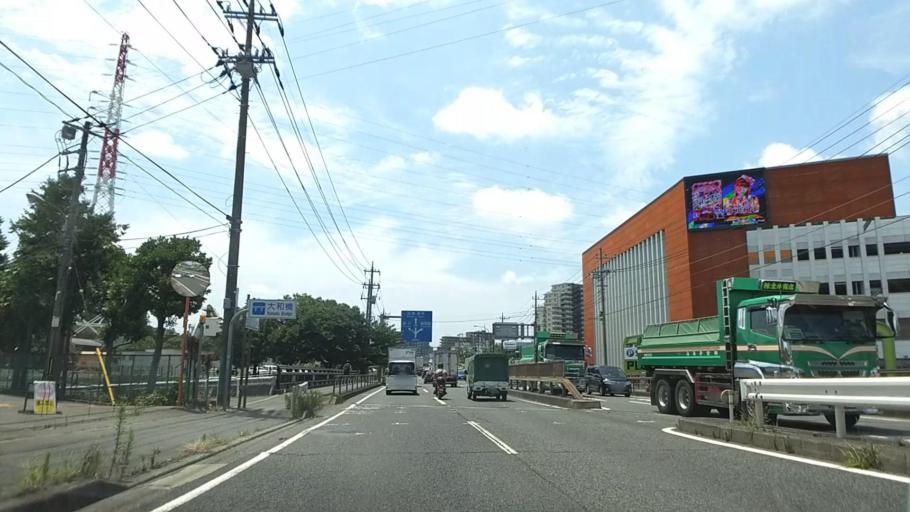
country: JP
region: Kanagawa
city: Minami-rinkan
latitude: 35.4963
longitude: 139.4658
